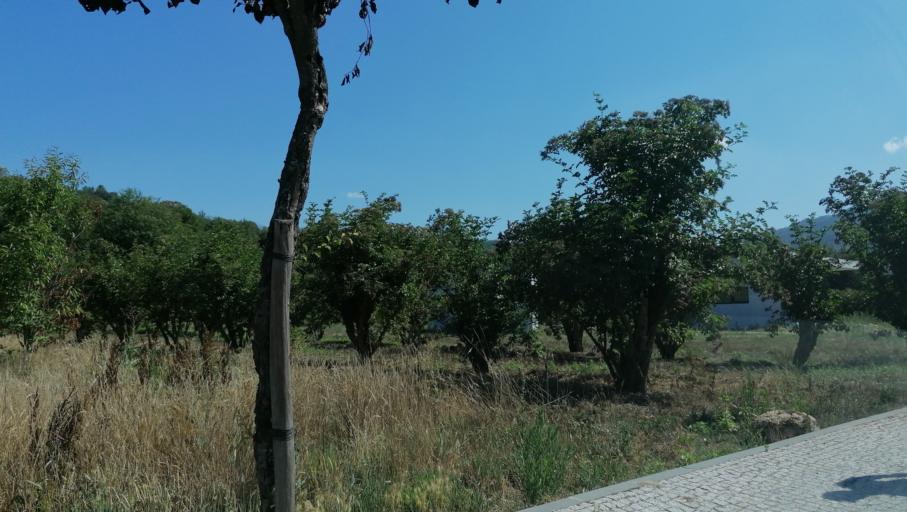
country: PT
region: Viseu
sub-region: Tarouca
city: Tarouca
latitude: 41.0242
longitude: -7.7668
